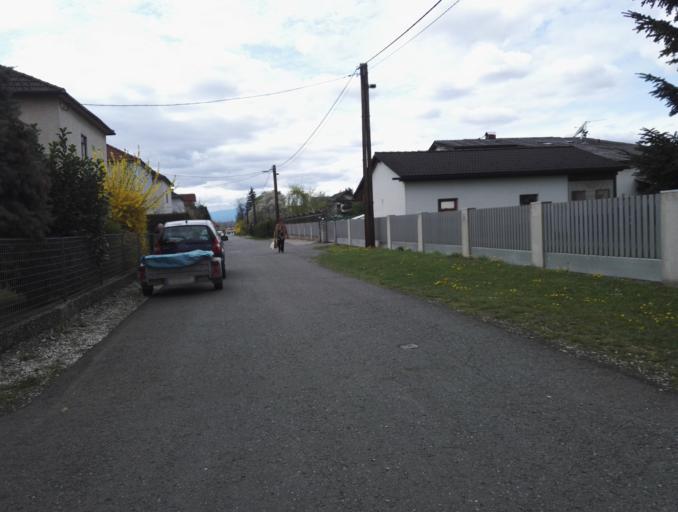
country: AT
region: Styria
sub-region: Politischer Bezirk Graz-Umgebung
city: Feldkirchen bei Graz
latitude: 47.0348
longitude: 15.4662
